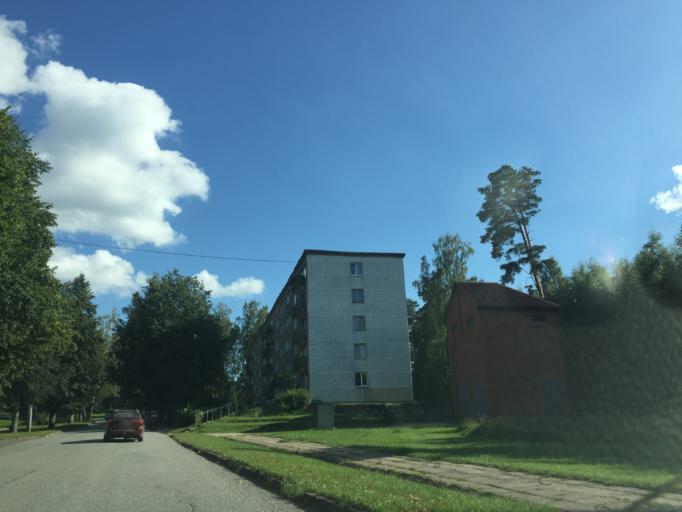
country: LV
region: Priekuli
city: Priekuli
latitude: 57.3854
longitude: 25.4240
